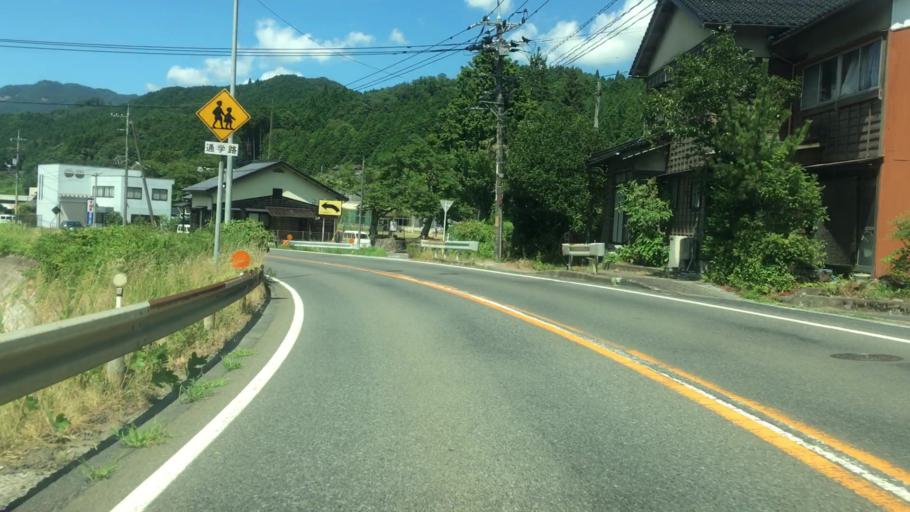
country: JP
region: Tottori
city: Tottori
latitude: 35.2388
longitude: 134.2288
